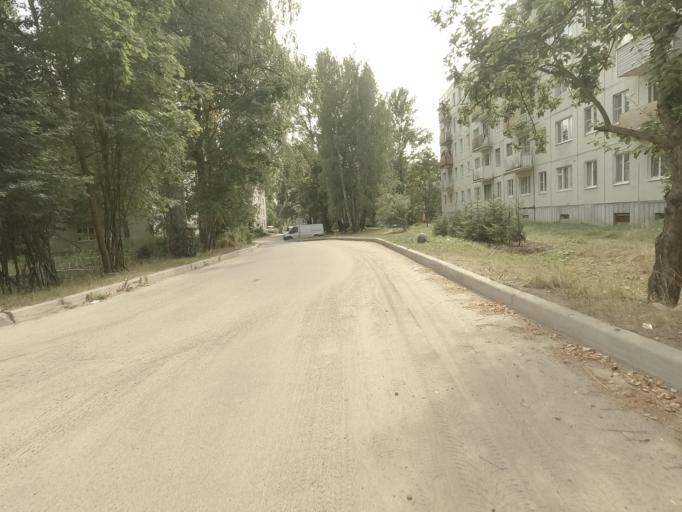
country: RU
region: Leningrad
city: Kamennogorsk
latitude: 60.9551
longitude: 29.1324
